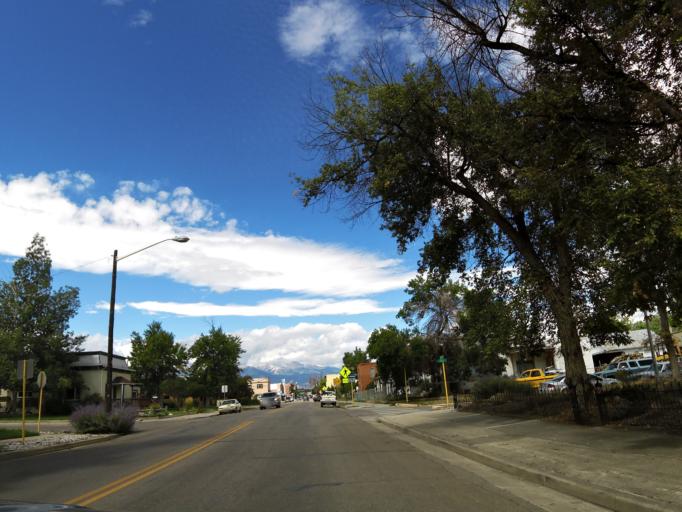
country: US
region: Colorado
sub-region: Chaffee County
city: Salida
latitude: 38.5342
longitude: -105.9883
